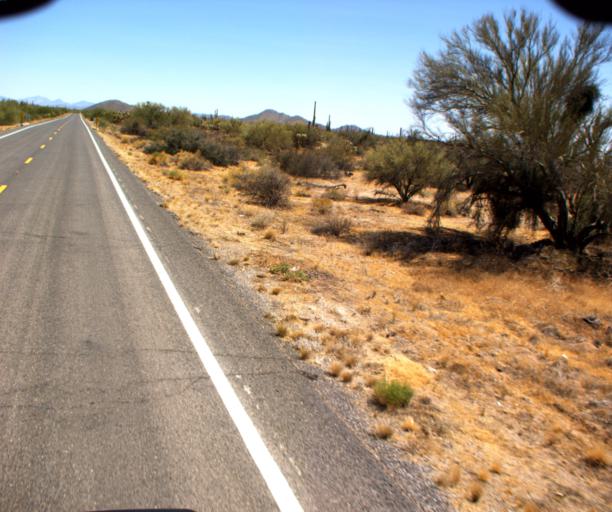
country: US
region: Arizona
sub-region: Pinal County
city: Florence
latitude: 32.7832
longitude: -111.1684
